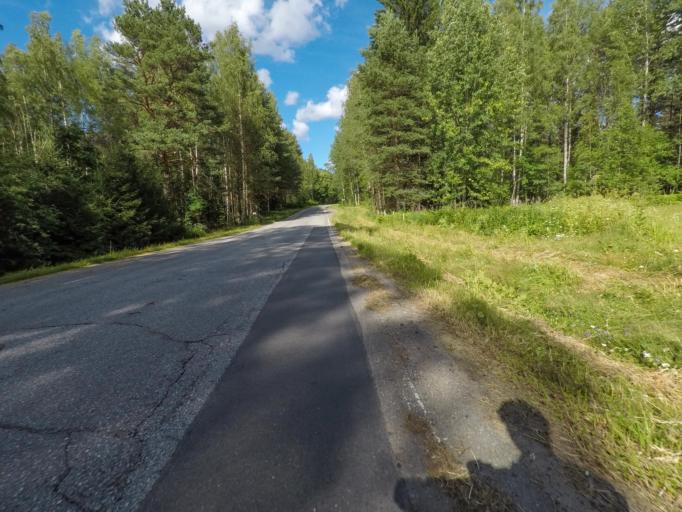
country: FI
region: South Karelia
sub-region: Lappeenranta
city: Joutseno
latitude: 61.1226
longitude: 28.3864
